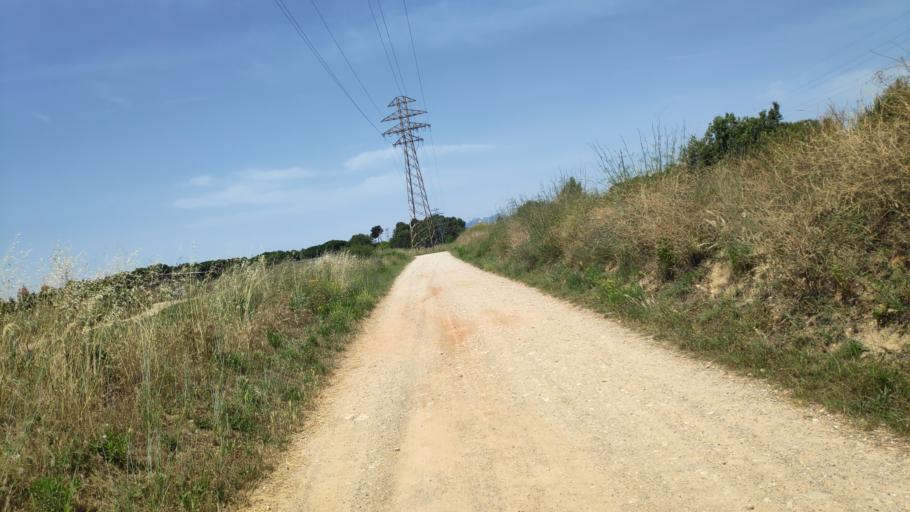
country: ES
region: Catalonia
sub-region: Provincia de Barcelona
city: Terrassa
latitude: 41.5654
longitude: 2.0572
